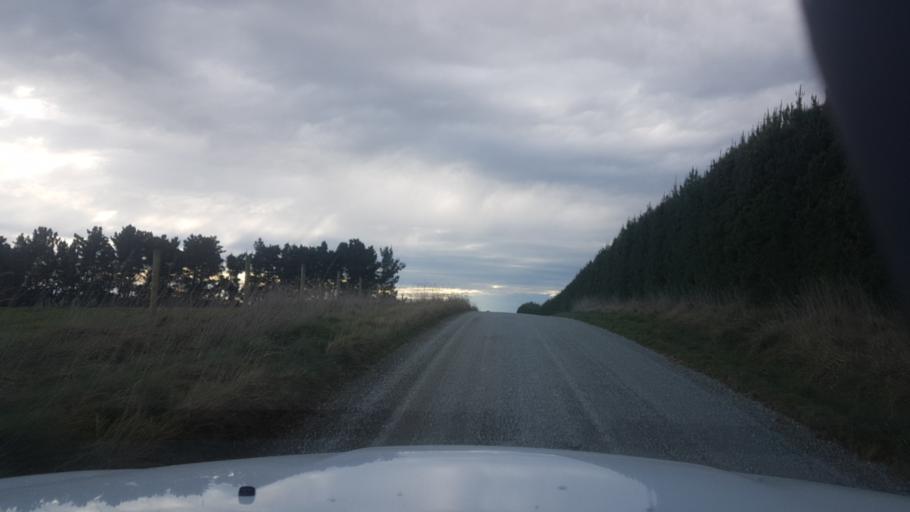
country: NZ
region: Canterbury
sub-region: Timaru District
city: Pleasant Point
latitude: -44.3413
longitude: 171.1426
